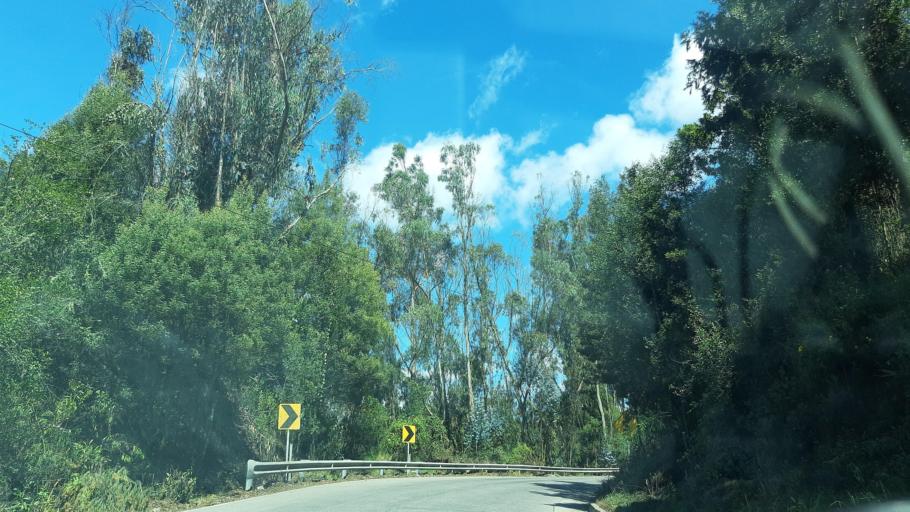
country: CO
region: Boyaca
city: Samaca
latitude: 5.4830
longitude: -73.4736
